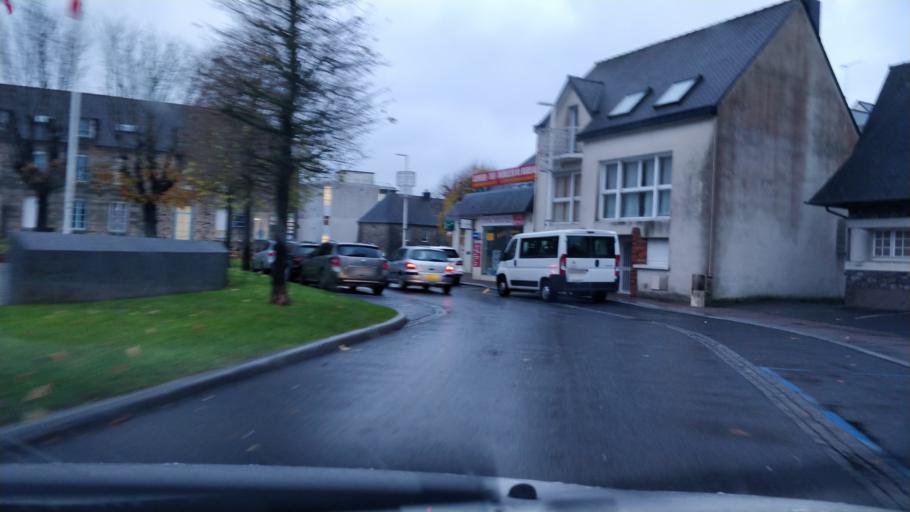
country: FR
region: Brittany
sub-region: Departement des Cotes-d'Armor
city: Loudeac
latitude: 48.1776
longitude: -2.7542
